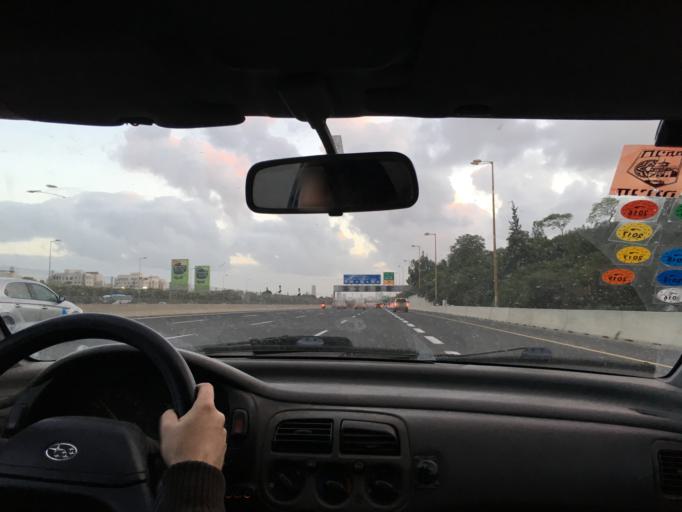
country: IL
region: Tel Aviv
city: Ramat HaSharon
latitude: 32.1282
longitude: 34.8099
